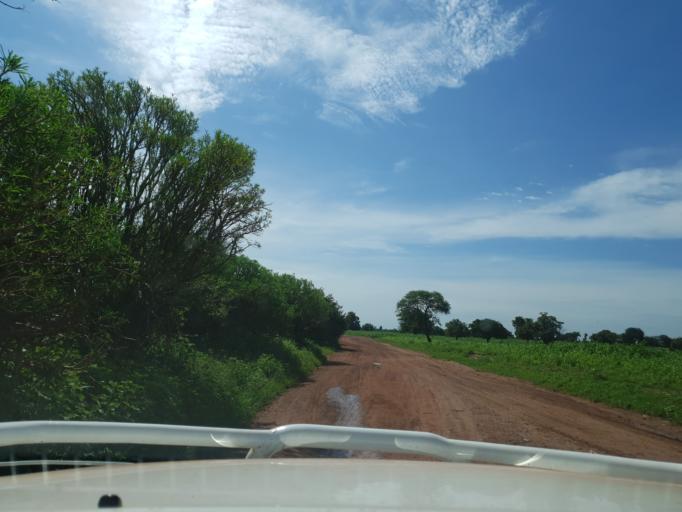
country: ML
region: Koulikoro
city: Banamba
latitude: 13.2771
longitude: -7.5476
